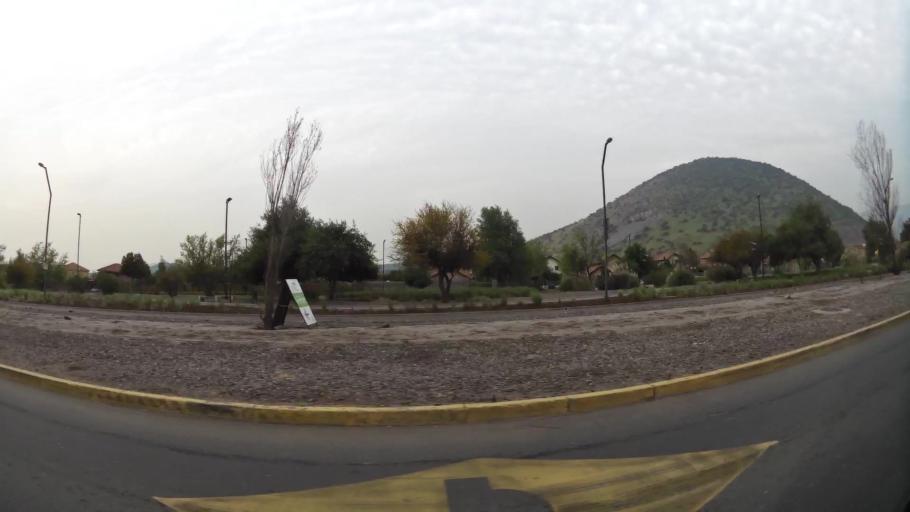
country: CL
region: Santiago Metropolitan
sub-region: Provincia de Chacabuco
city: Chicureo Abajo
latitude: -33.3108
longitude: -70.6587
